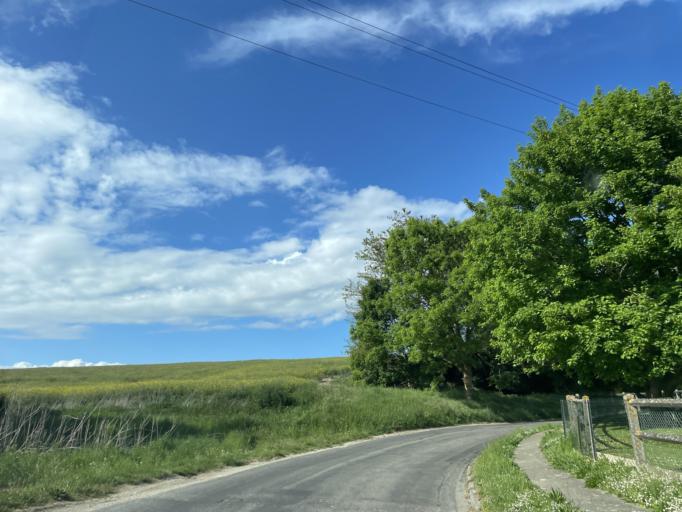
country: FR
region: Ile-de-France
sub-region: Departement de Seine-et-Marne
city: Charny
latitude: 48.9493
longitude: 2.7792
